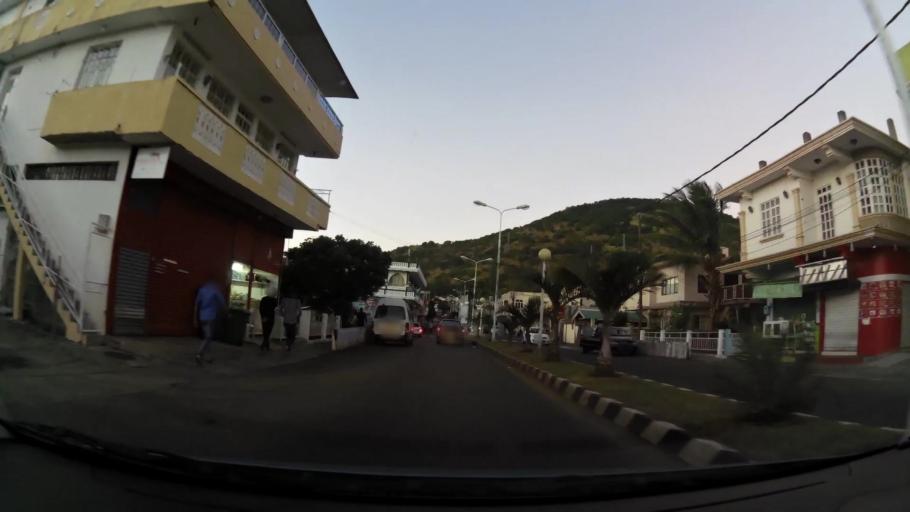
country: MU
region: Port Louis
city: Port Louis
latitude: -20.1664
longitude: 57.5167
